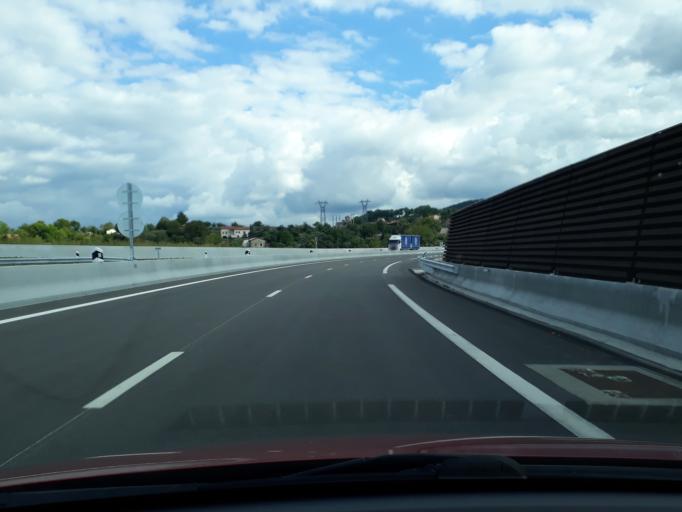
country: FR
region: Auvergne
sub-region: Departement de la Haute-Loire
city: Chadrac
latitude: 45.0434
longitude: 3.9082
